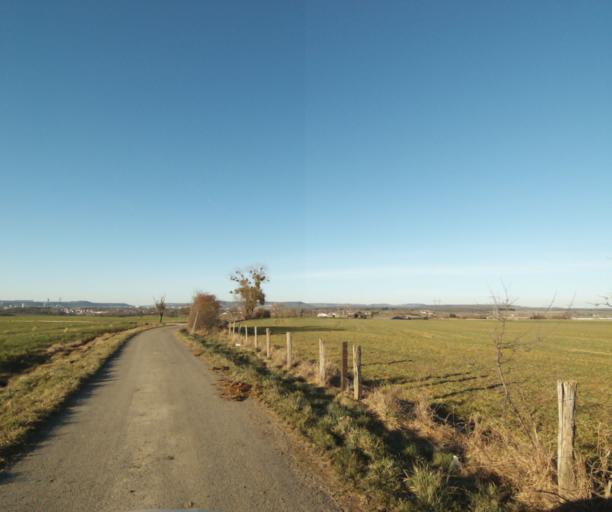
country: FR
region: Lorraine
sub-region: Departement de Meurthe-et-Moselle
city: Laneuveville-devant-Nancy
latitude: 48.6369
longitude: 6.2316
